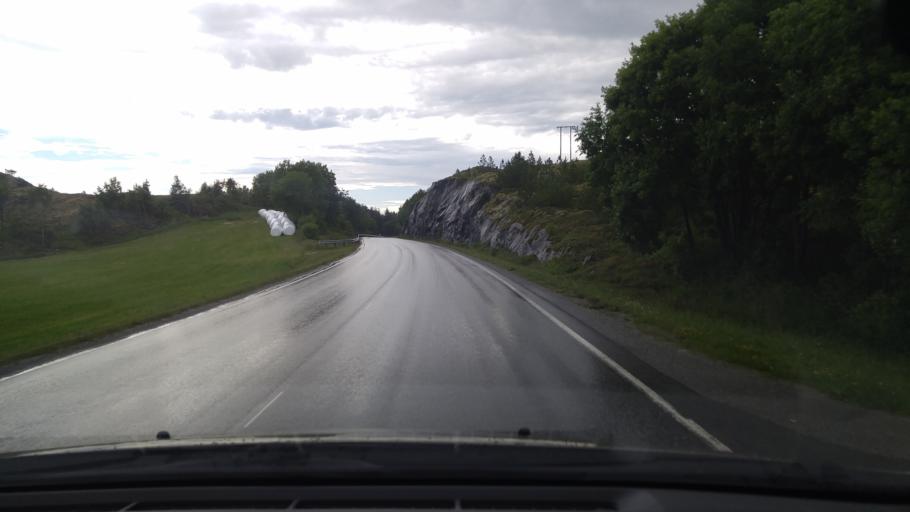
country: NO
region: Nord-Trondelag
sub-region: Vikna
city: Rorvik
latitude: 64.8445
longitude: 11.2848
